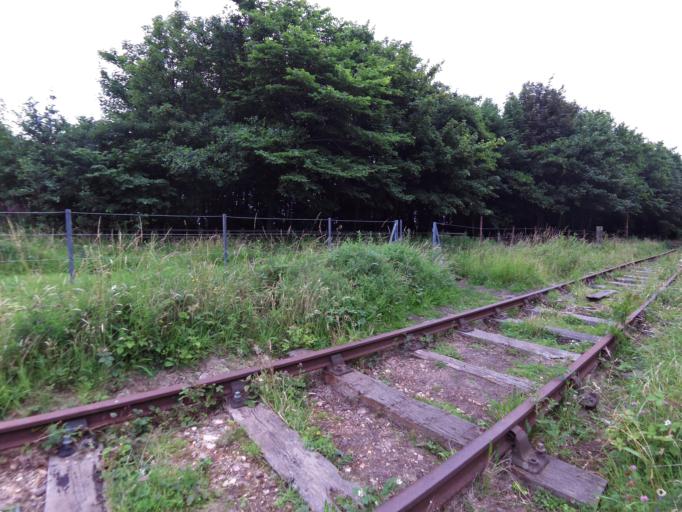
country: GB
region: Scotland
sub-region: East Lothian
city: Prestonpans
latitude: 55.9526
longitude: -3.0038
